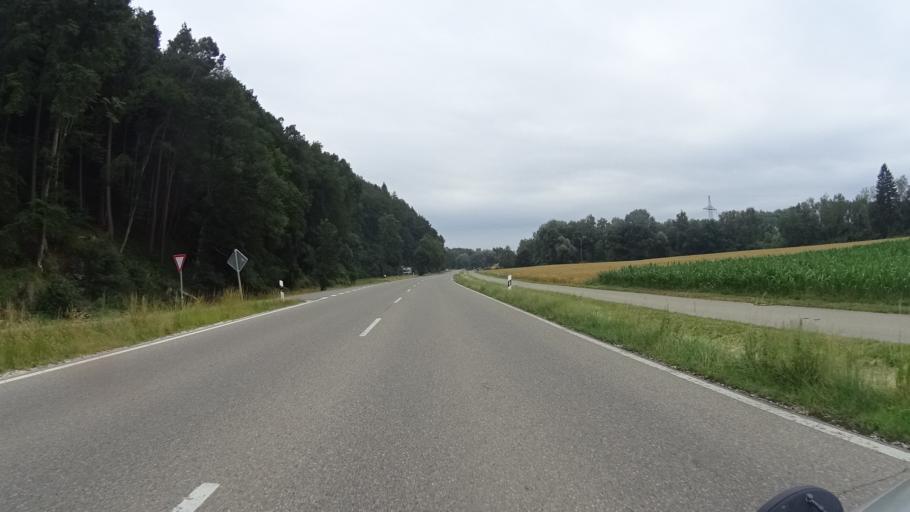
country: DE
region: Bavaria
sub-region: Swabia
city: Kellmunz
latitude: 48.1345
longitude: 10.1193
